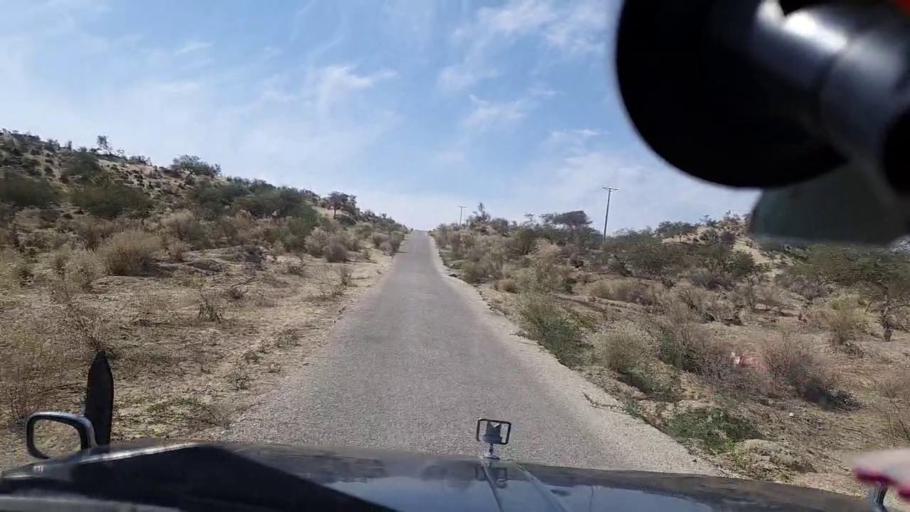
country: PK
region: Sindh
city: Diplo
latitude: 24.3846
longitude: 69.5868
